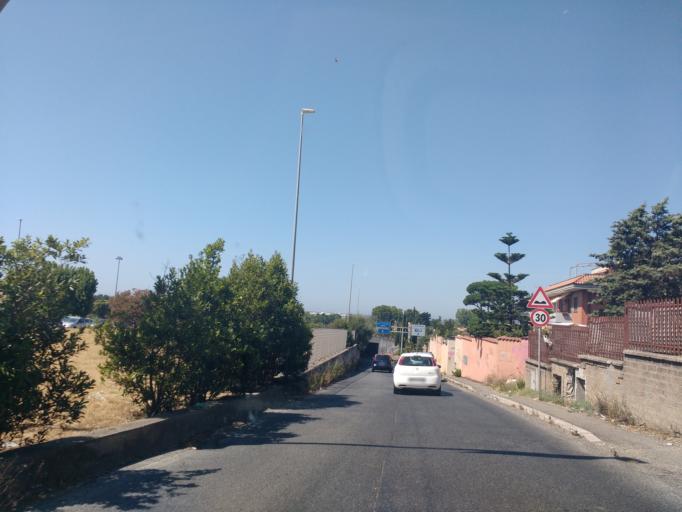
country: IT
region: Latium
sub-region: Citta metropolitana di Roma Capitale
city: Acilia-Castel Fusano-Ostia Antica
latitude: 41.7838
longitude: 12.3594
